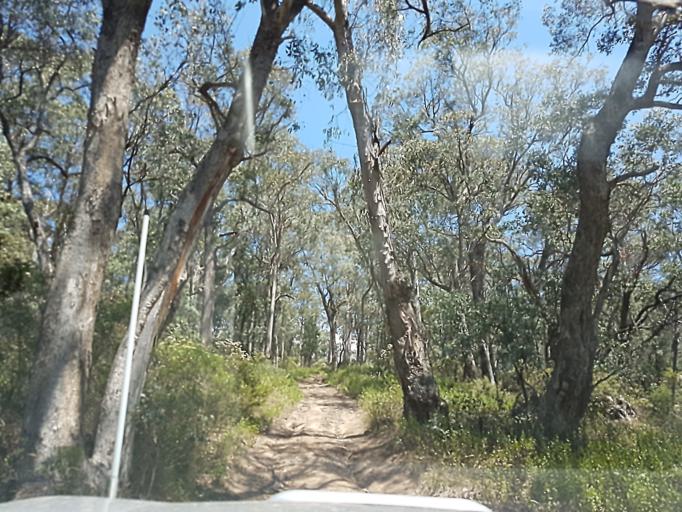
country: AU
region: Victoria
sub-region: East Gippsland
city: Lakes Entrance
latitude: -37.3102
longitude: 148.3575
